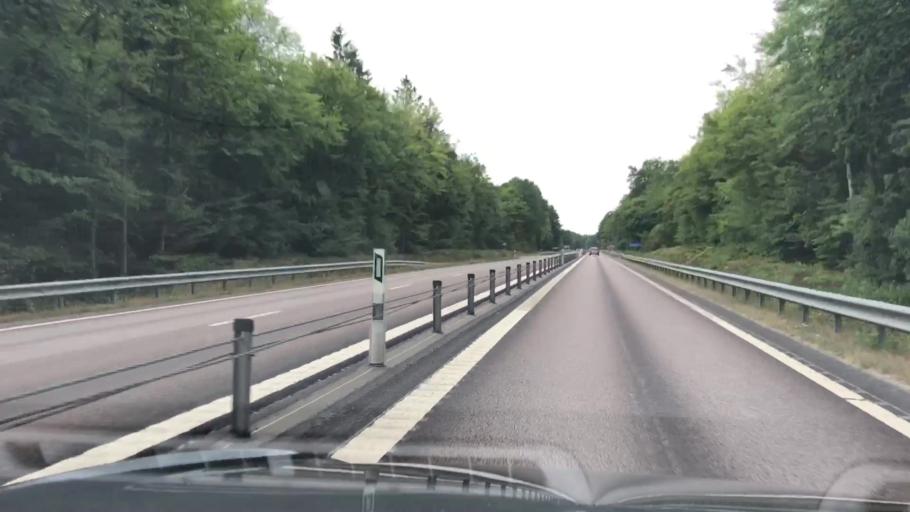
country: SE
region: Blekinge
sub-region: Karlskrona Kommun
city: Jaemjoe
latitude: 56.2339
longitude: 15.9197
